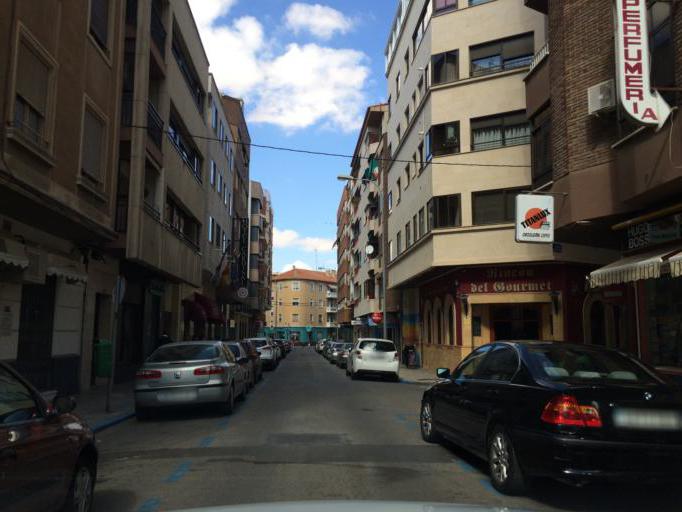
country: ES
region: Castille-La Mancha
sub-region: Provincia de Albacete
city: Albacete
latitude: 38.9944
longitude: -1.8604
